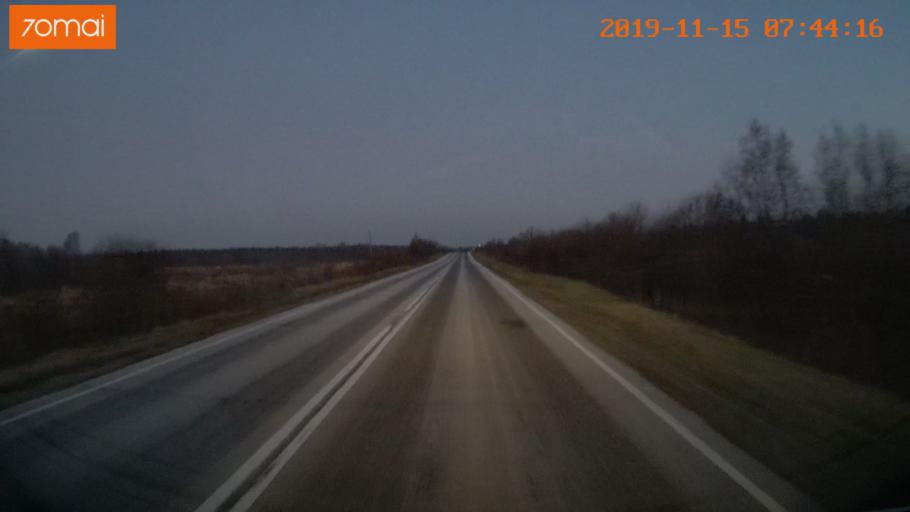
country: RU
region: Vologda
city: Sheksna
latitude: 58.8117
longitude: 38.3151
